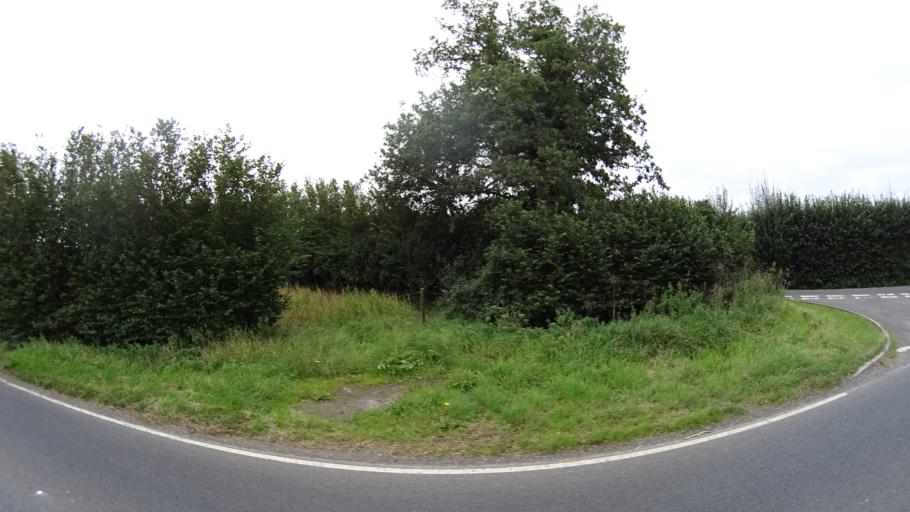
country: GB
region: England
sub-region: Somerset
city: Wincanton
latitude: 51.0598
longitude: -2.3474
